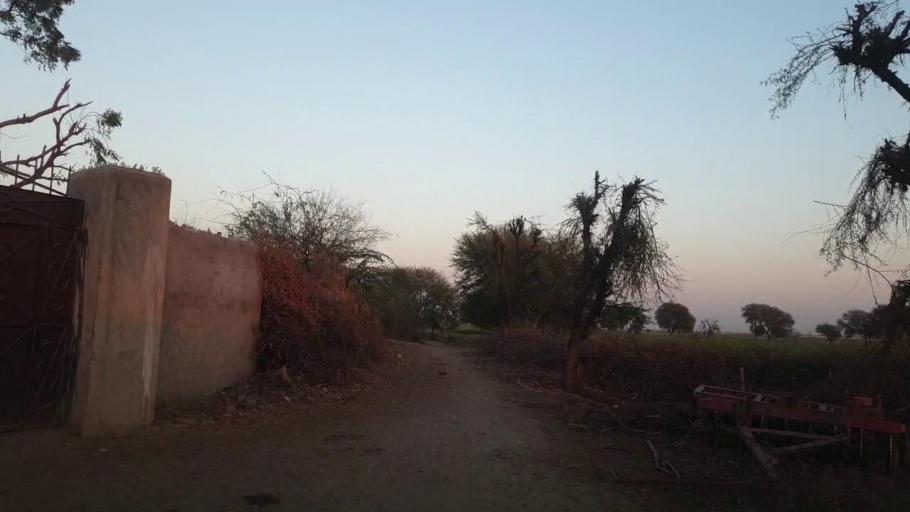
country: PK
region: Sindh
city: Mirpur Khas
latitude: 25.6909
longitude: 69.0558
